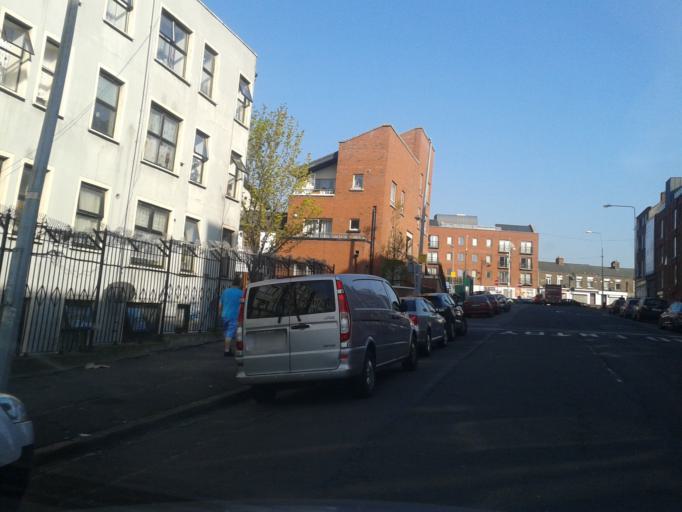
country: IE
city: Fairview
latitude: 53.3555
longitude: -6.2505
